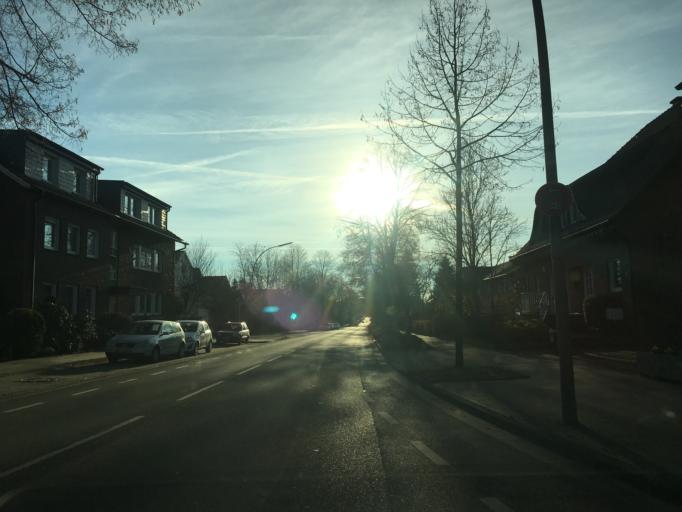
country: DE
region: North Rhine-Westphalia
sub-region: Regierungsbezirk Munster
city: Muenster
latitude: 51.9523
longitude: 7.5313
